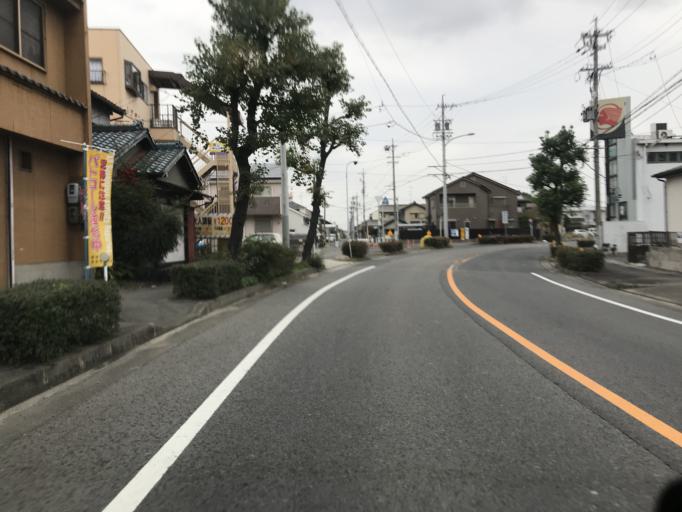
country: JP
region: Aichi
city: Inazawa
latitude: 35.2079
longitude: 136.8398
